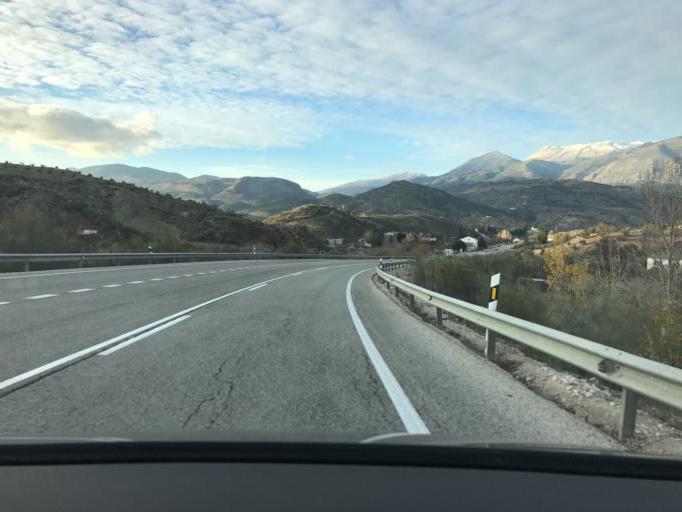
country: ES
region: Andalusia
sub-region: Provincia de Jaen
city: Huelma
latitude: 37.6406
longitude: -3.4147
